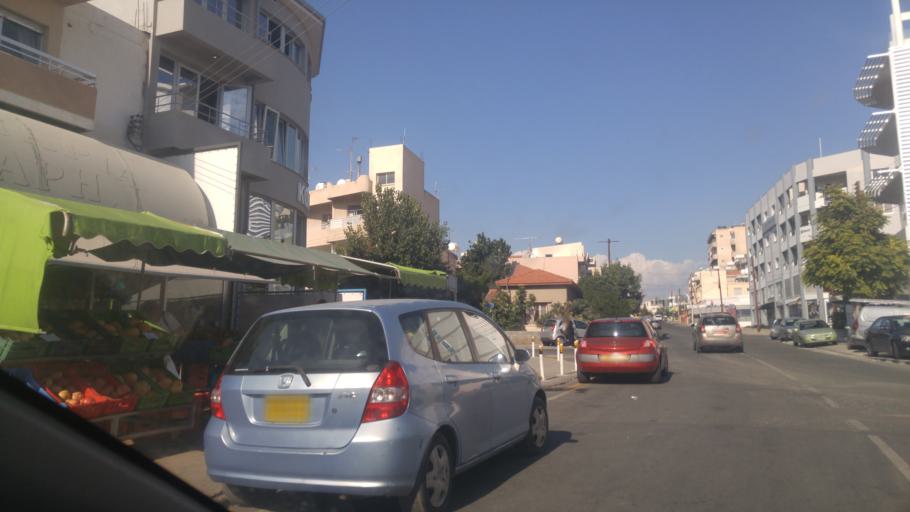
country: CY
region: Limassol
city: Limassol
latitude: 34.6967
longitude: 33.0499
